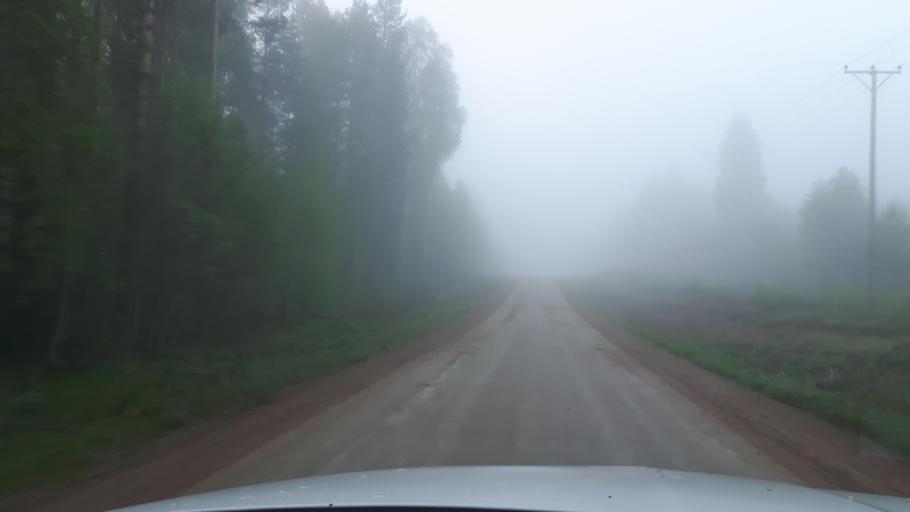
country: SE
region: Vaesternorrland
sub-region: Ange Kommun
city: Ange
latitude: 62.1622
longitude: 15.6591
